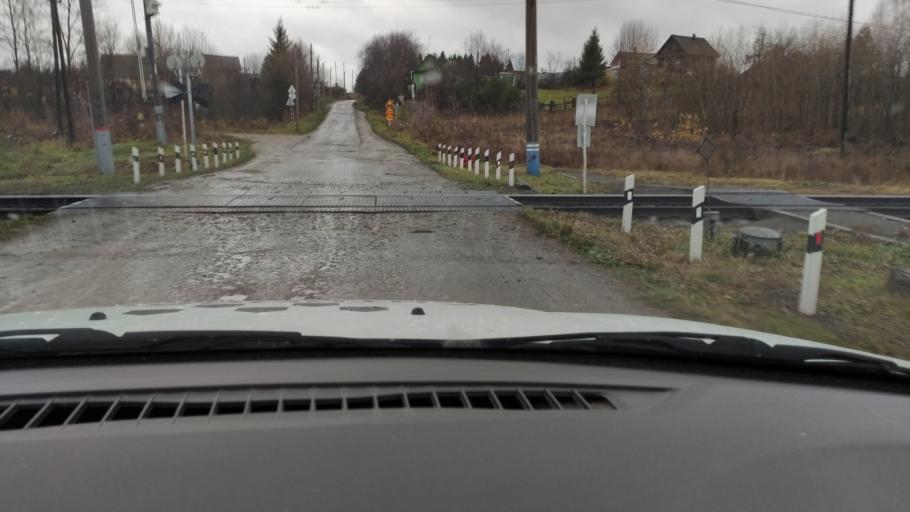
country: RU
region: Perm
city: Sylva
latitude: 58.0420
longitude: 56.7499
